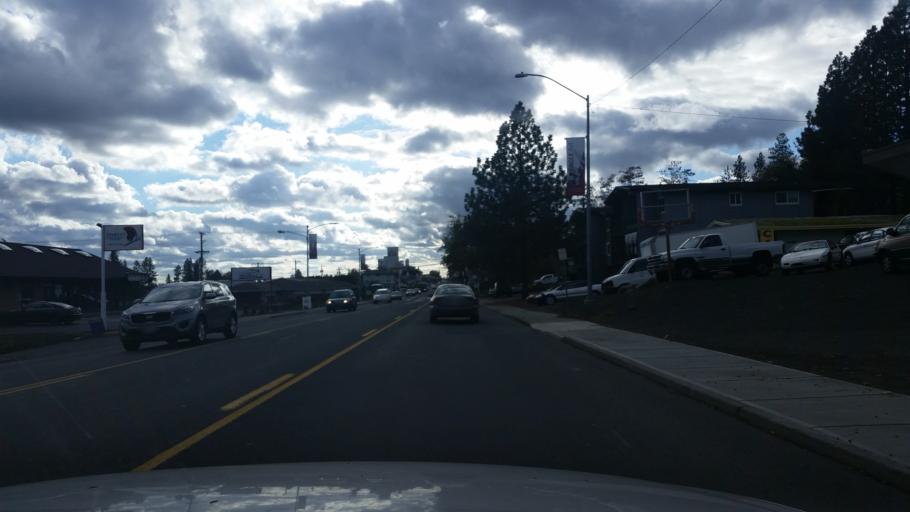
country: US
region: Washington
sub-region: Spokane County
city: Cheney
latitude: 47.4943
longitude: -117.5672
